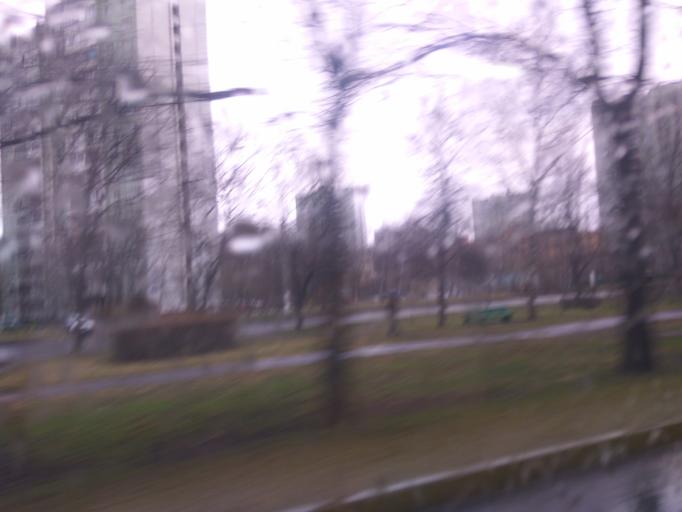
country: RU
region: Moscow
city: Bibirevo
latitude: 55.8970
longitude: 37.6086
